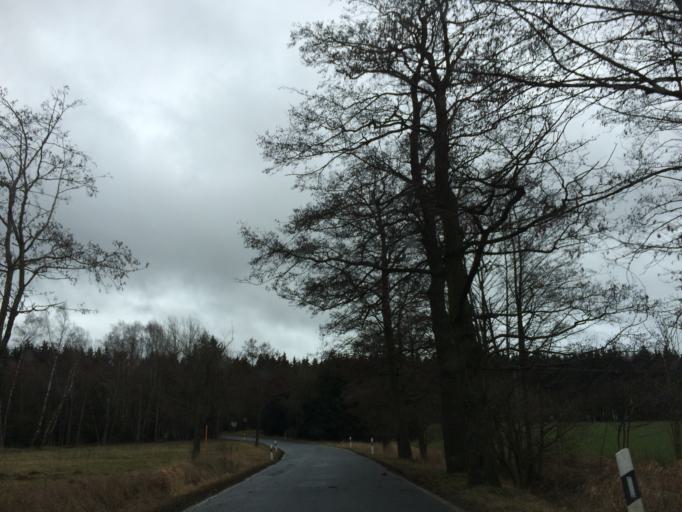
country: DE
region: Thuringia
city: Quaschwitz
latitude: 50.6747
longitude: 11.7102
